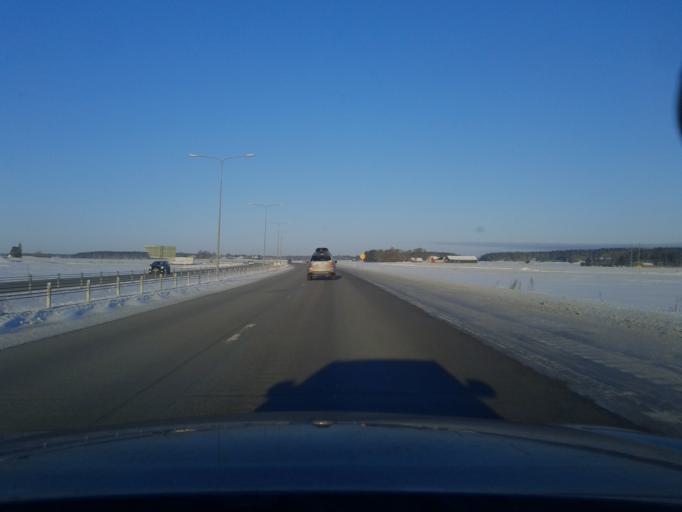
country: SE
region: Uppsala
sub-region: Uppsala Kommun
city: Saevja
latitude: 59.8508
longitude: 17.7340
